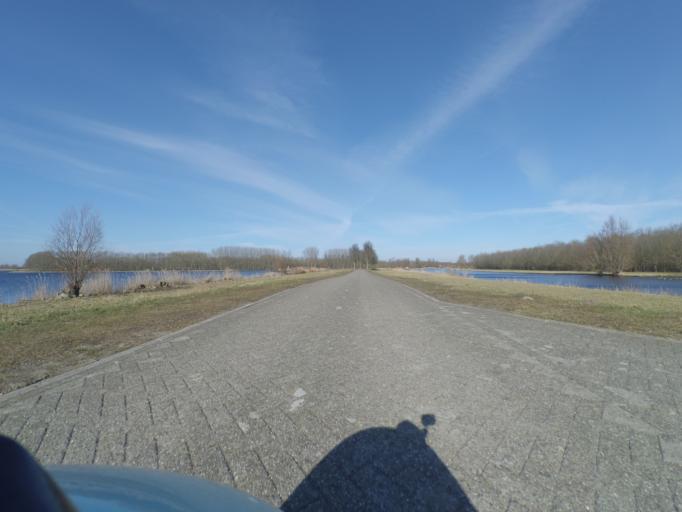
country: NL
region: Flevoland
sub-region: Gemeente Almere
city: Almere Stad
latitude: 52.3993
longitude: 5.2295
